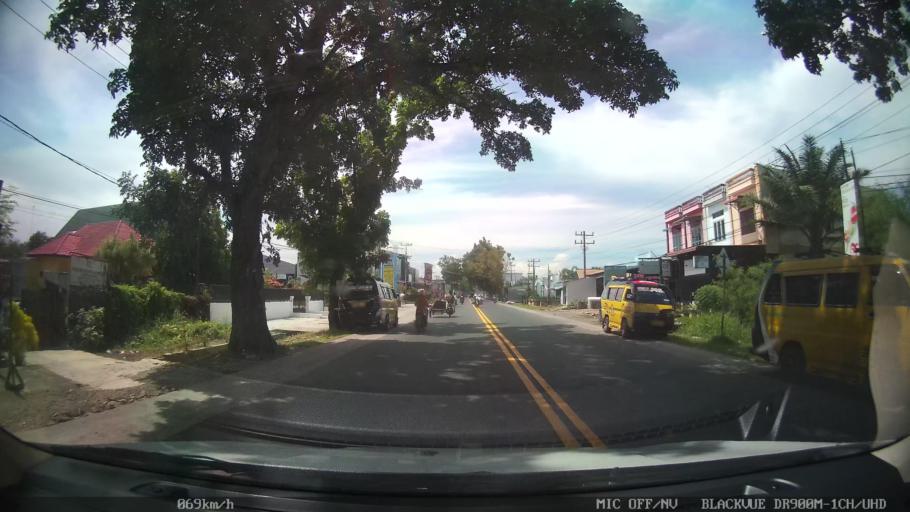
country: ID
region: North Sumatra
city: Binjai
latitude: 3.6470
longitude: 98.5102
